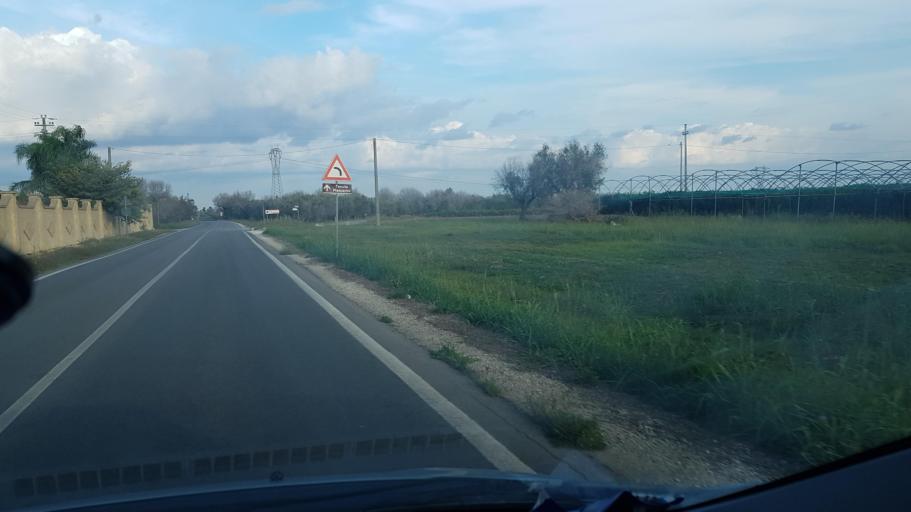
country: IT
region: Apulia
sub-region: Provincia di Lecce
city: Veglie
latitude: 40.3393
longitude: 18.0007
